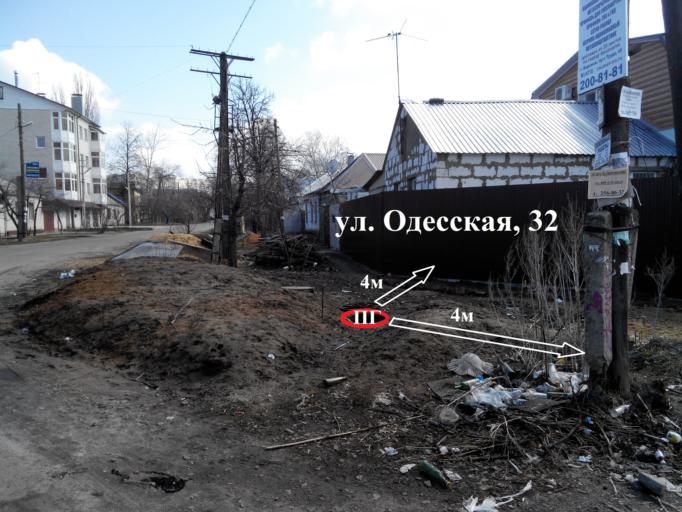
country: RU
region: Voronezj
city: Voronezh
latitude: 51.6316
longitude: 39.1728
